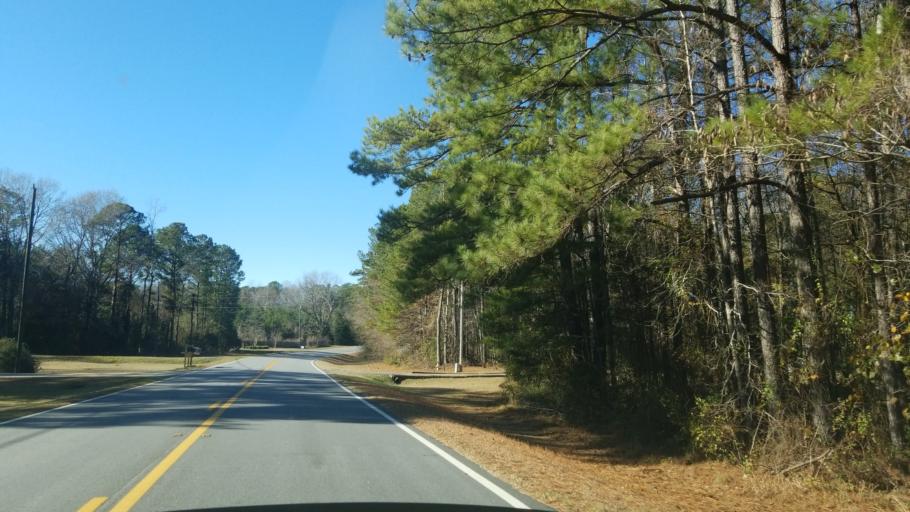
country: US
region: Georgia
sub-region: Harris County
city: Hamilton
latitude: 32.6701
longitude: -84.9023
